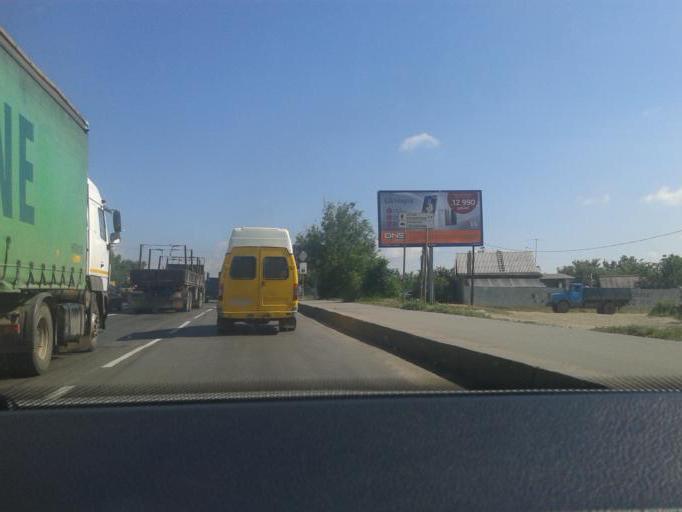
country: RU
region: Volgograd
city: Volgograd
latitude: 48.6702
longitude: 44.4422
